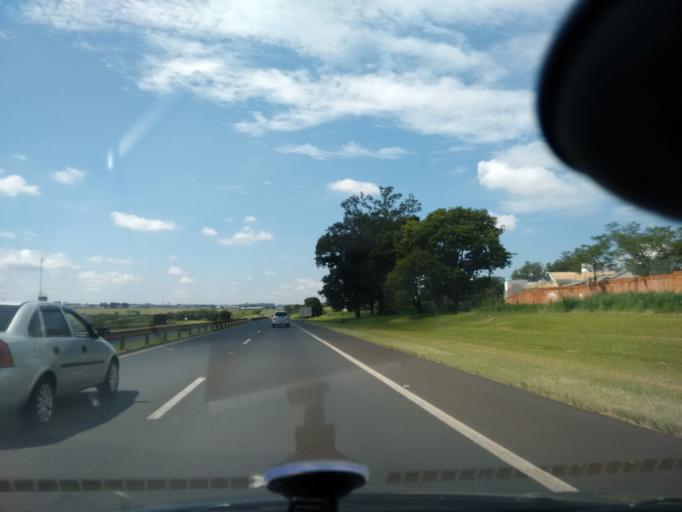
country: BR
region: Sao Paulo
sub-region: Sao Carlos
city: Sao Carlos
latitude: -21.9786
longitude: -47.9259
